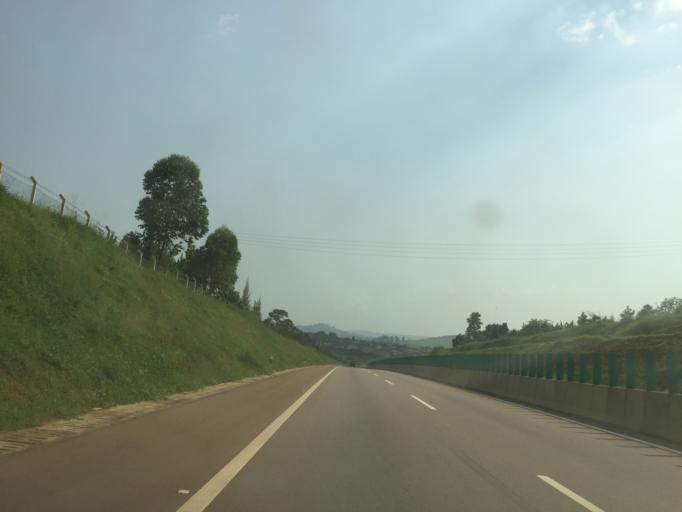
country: UG
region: Central Region
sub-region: Wakiso District
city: Kajansi
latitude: 0.2447
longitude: 32.5235
